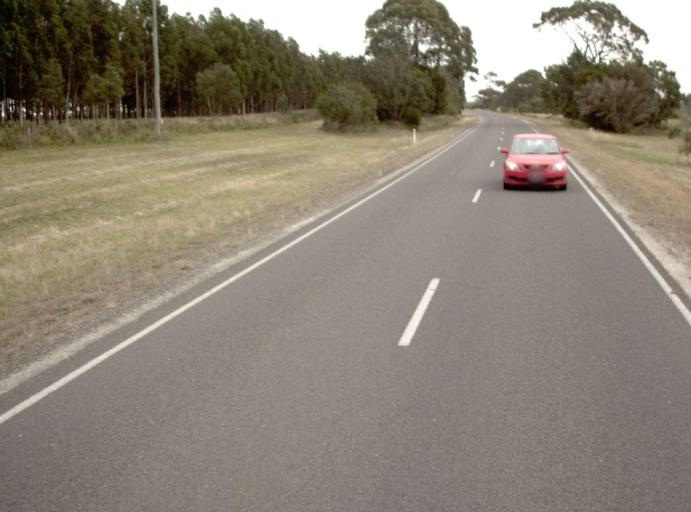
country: AU
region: Victoria
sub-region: Wellington
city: Sale
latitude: -38.1953
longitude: 147.2907
